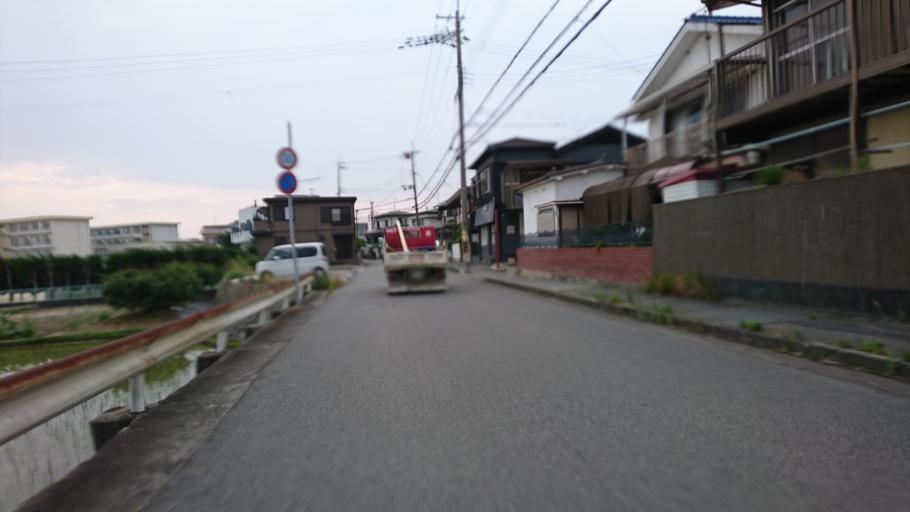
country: JP
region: Hyogo
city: Kakogawacho-honmachi
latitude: 34.7596
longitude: 134.8728
